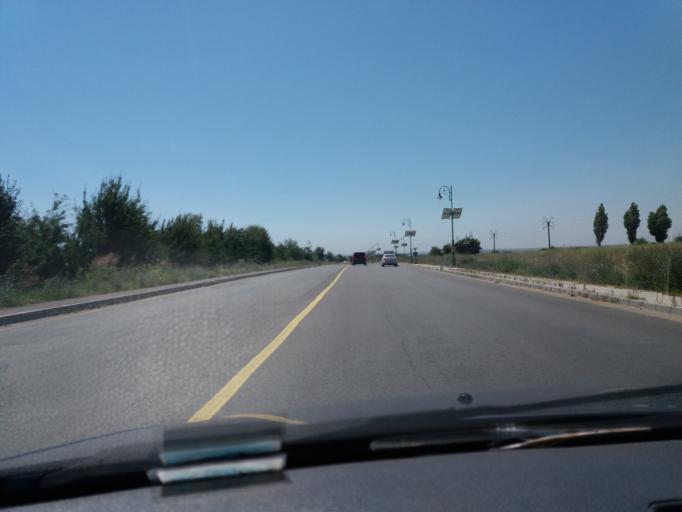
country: RO
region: Constanta
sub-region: Comuna Navodari
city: Navodari
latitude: 44.2989
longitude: 28.6138
